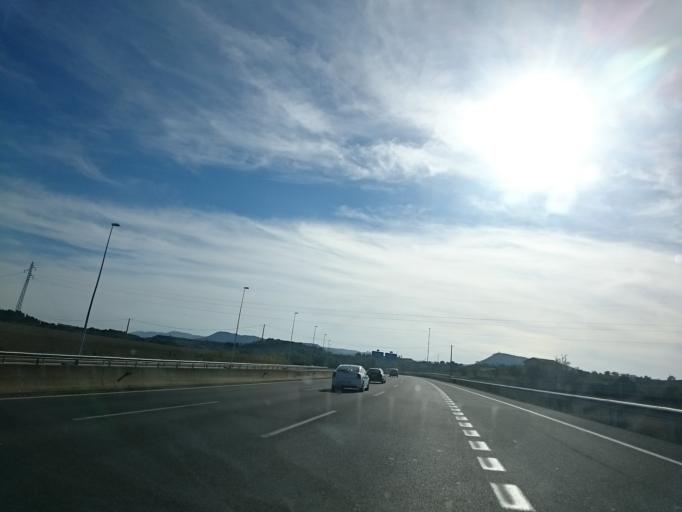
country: ES
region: Catalonia
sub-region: Provincia de Barcelona
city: Gurb
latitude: 41.9505
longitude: 2.2344
